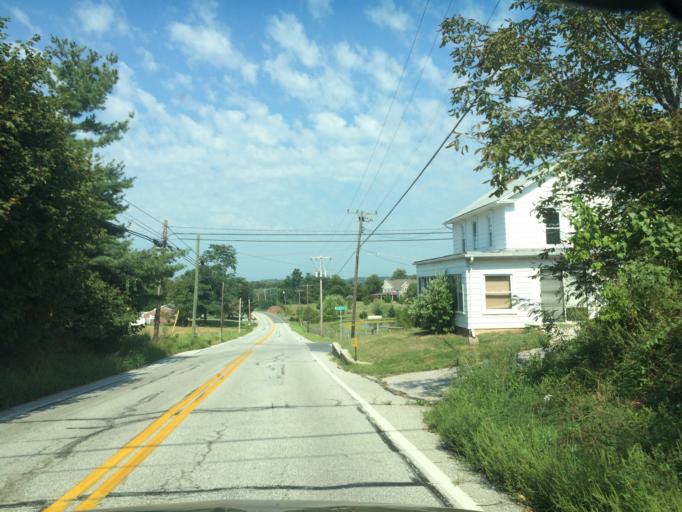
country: US
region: Maryland
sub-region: Carroll County
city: Taneytown
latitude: 39.6265
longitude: -77.1096
